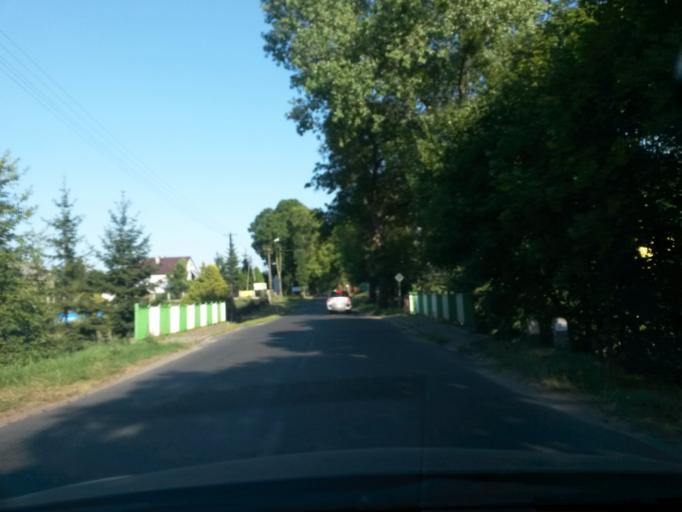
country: PL
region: Kujawsko-Pomorskie
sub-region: Powiat rypinski
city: Skrwilno
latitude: 53.0581
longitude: 19.6087
